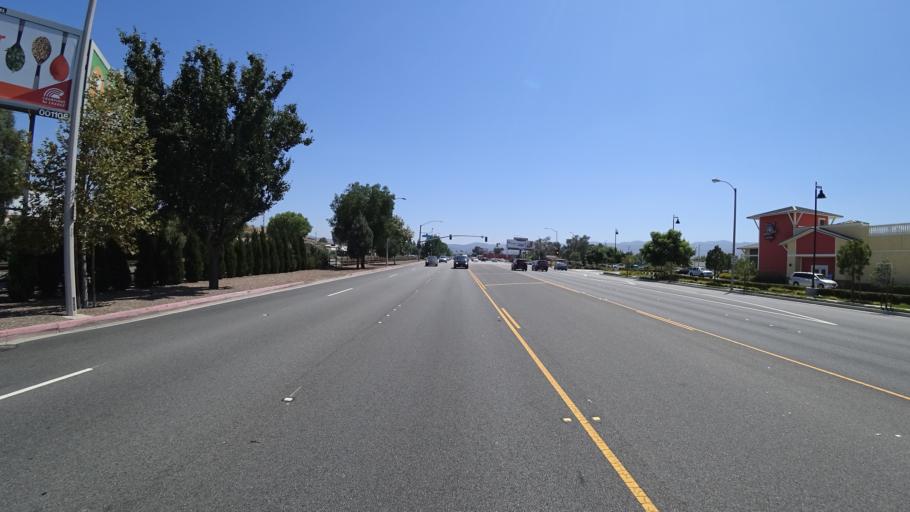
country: US
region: California
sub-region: Los Angeles County
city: Santa Clarita
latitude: 34.4146
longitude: -118.5412
